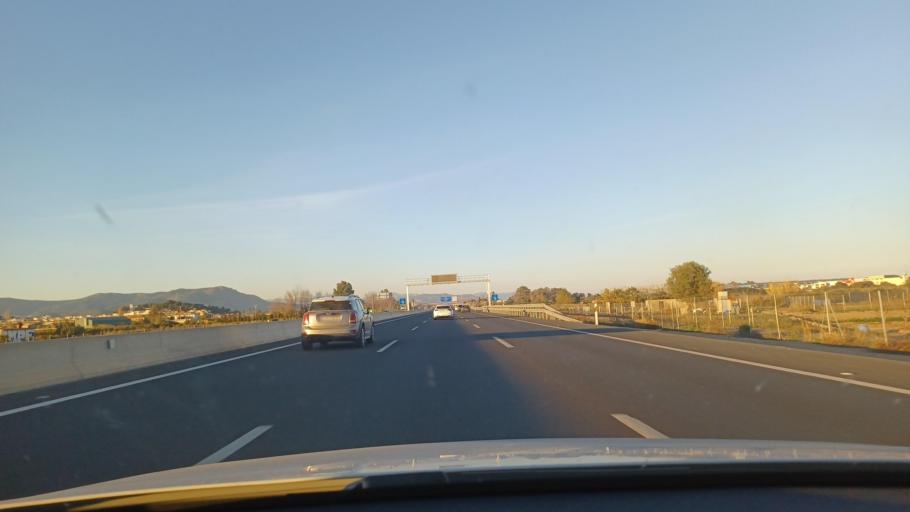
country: ES
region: Valencia
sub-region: Provincia de Valencia
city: Puig
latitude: 39.5782
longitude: -0.2946
